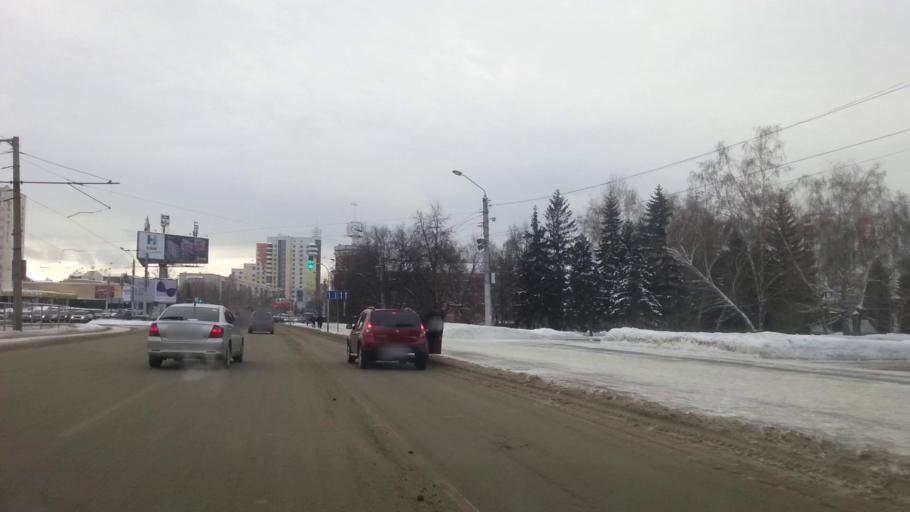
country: RU
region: Altai Krai
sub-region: Gorod Barnaulskiy
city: Barnaul
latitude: 53.3498
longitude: 83.7619
